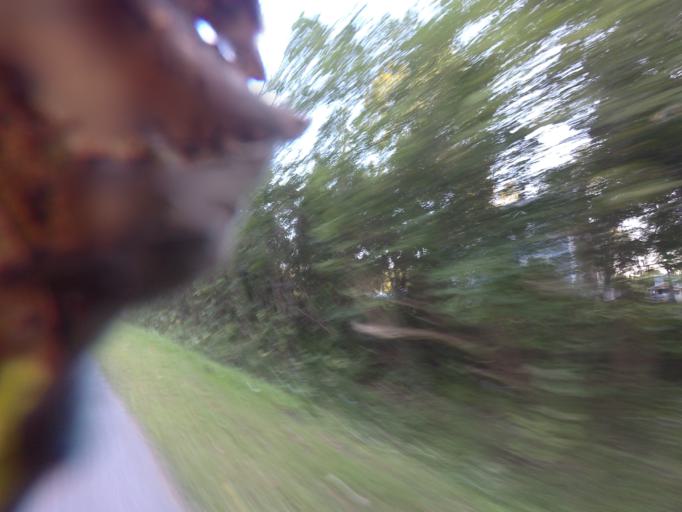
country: CA
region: Quebec
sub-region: Monteregie
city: Hudson
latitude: 45.4741
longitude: -74.1869
